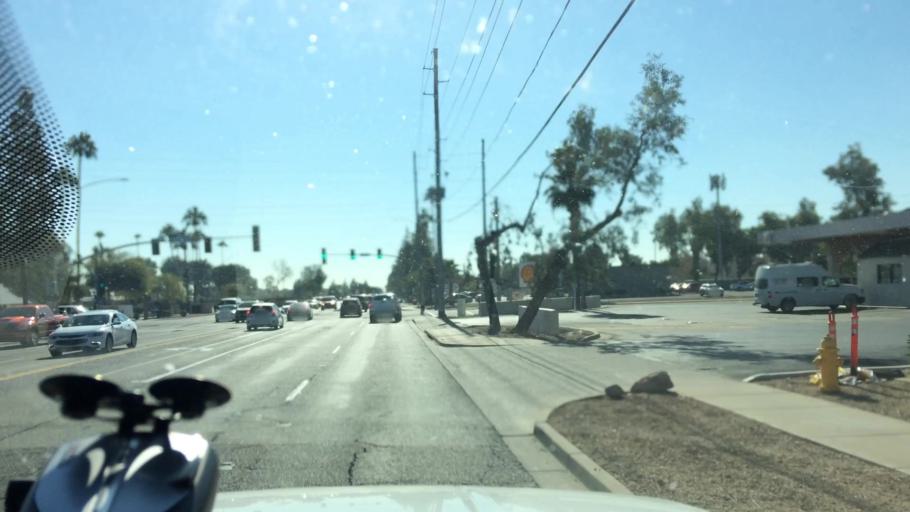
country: US
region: Arizona
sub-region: Maricopa County
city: Peoria
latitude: 33.6259
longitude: -112.1858
